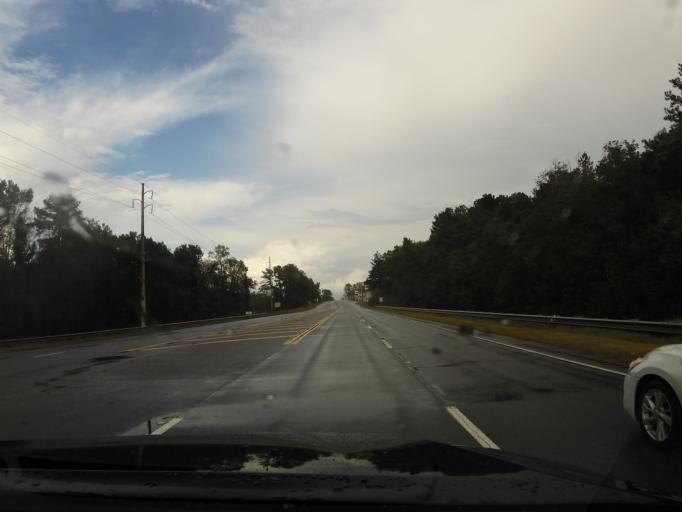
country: US
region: Georgia
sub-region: Long County
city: Ludowici
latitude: 31.7072
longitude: -81.7571
